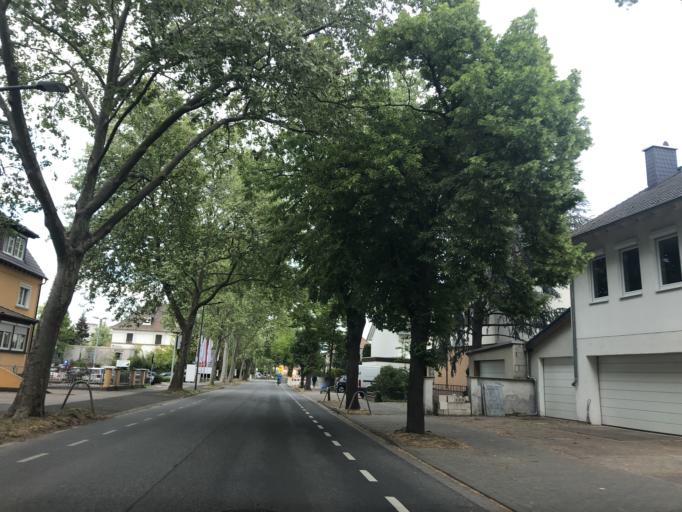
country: DE
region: Rheinland-Pfalz
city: Frankenthal
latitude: 49.5438
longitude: 8.3670
